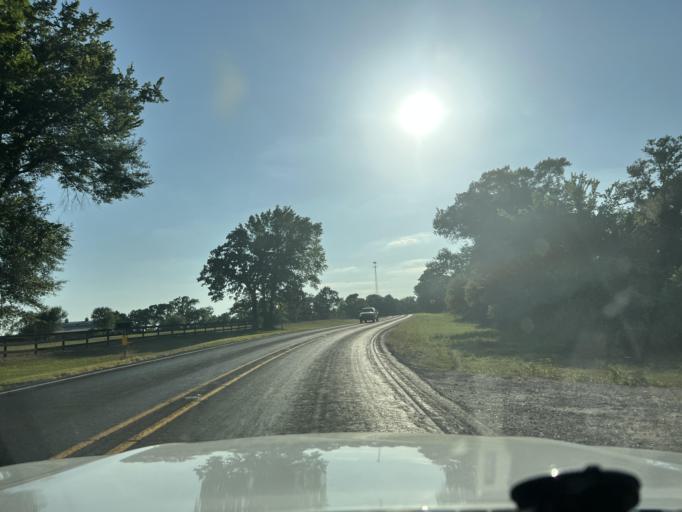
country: US
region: Texas
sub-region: Washington County
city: Brenham
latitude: 30.2337
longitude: -96.2804
